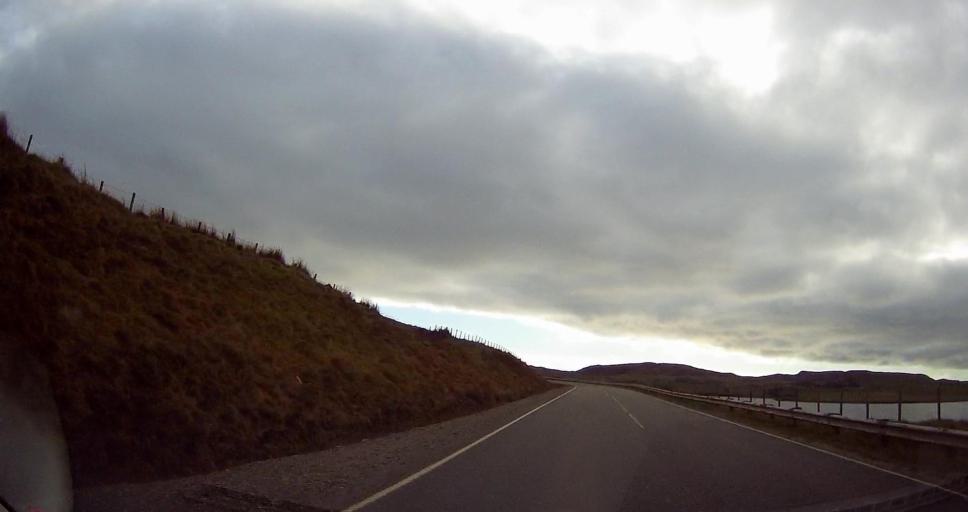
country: GB
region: Scotland
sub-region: Shetland Islands
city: Lerwick
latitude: 60.4077
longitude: -1.3386
